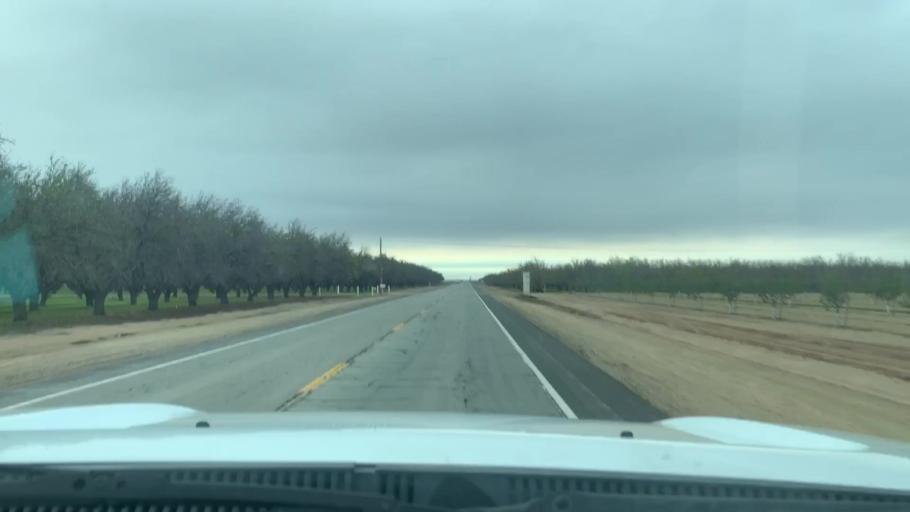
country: US
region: California
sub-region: Kern County
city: Rosedale
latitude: 35.4787
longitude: -119.1532
